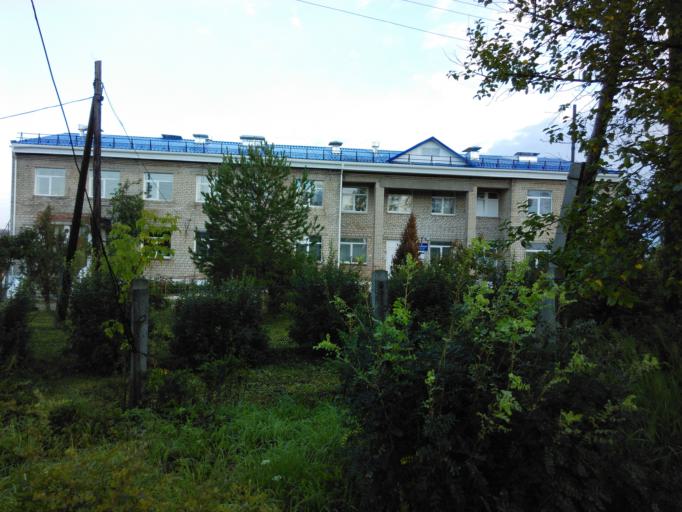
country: RU
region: Perm
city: Foki
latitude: 56.7024
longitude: 54.3570
